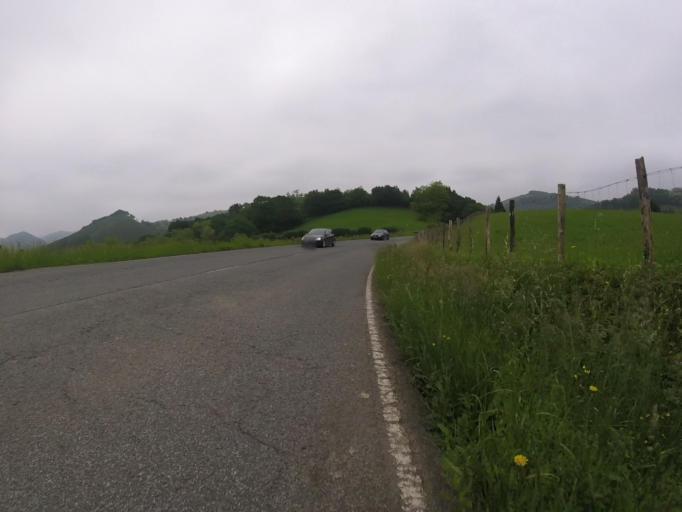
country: ES
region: Navarre
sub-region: Provincia de Navarra
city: Zugarramurdi
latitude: 43.2747
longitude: -1.4970
